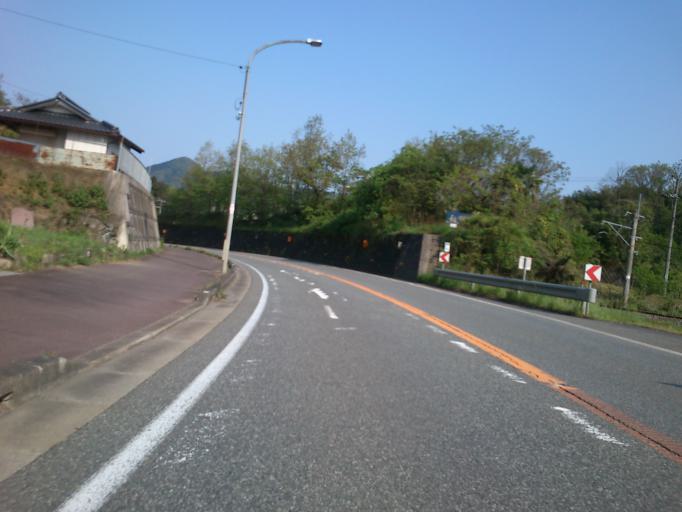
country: JP
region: Kyoto
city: Fukuchiyama
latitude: 35.3233
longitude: 135.0453
